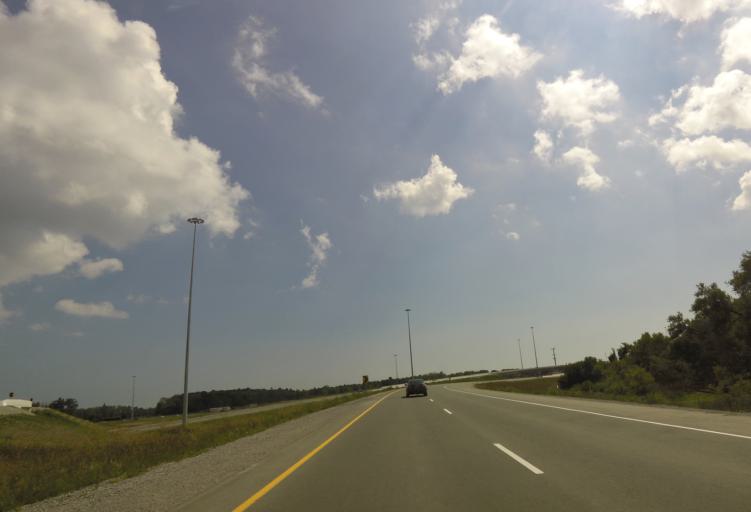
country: CA
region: Ontario
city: Ajax
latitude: 43.8687
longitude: -78.9757
